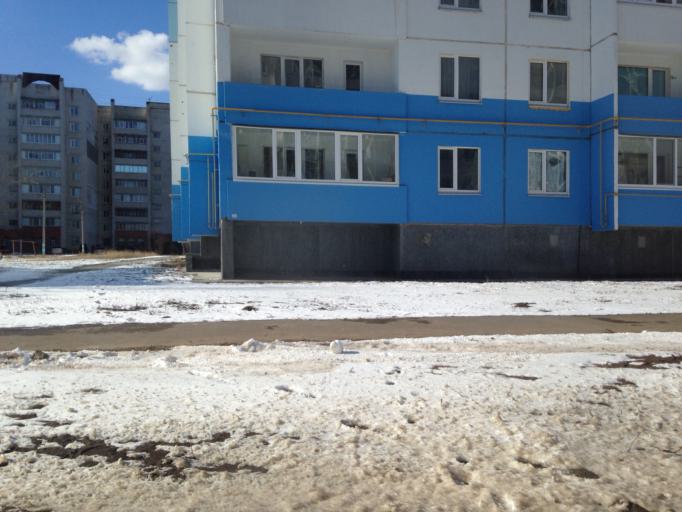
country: RU
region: Ulyanovsk
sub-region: Ulyanovskiy Rayon
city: Ulyanovsk
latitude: 54.3263
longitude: 48.4719
